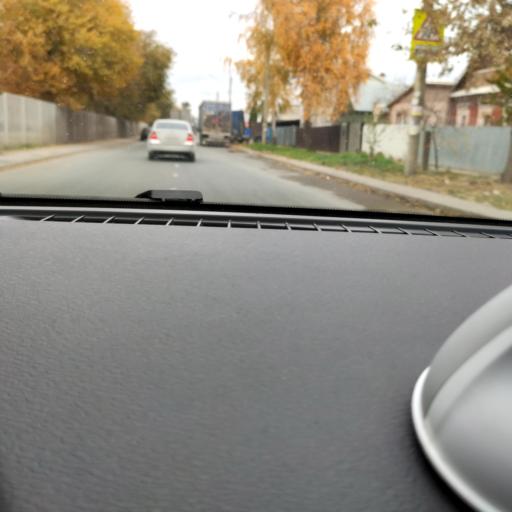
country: RU
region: Samara
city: Smyshlyayevka
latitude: 53.2305
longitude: 50.3090
